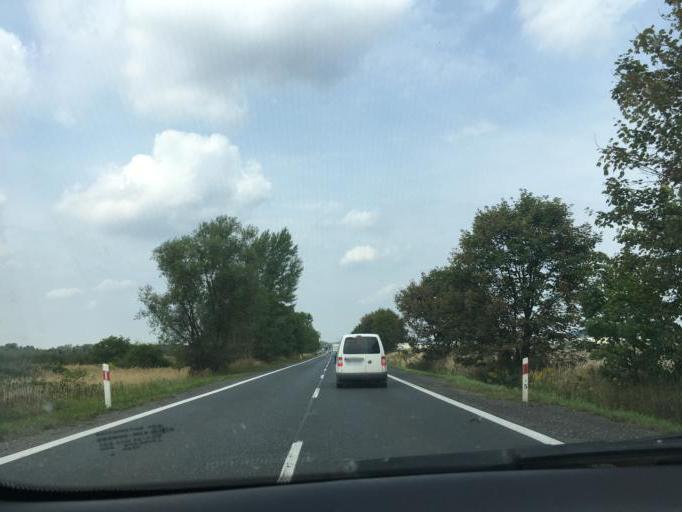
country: PL
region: Silesian Voivodeship
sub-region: Powiat bierunsko-ledzinski
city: Bierun
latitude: 50.0879
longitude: 19.1085
